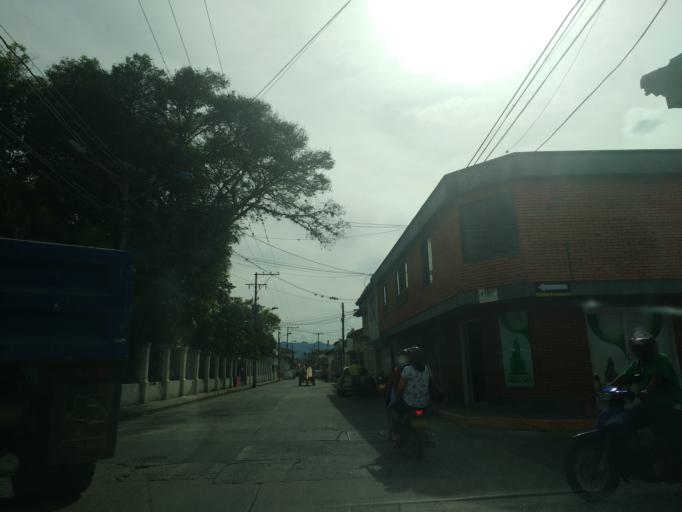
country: CO
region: Valle del Cauca
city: Cartago
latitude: 4.7484
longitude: -75.9092
